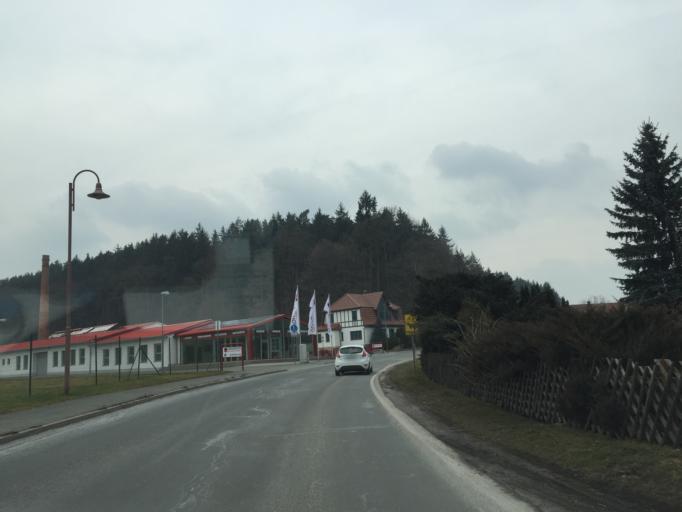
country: DE
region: Thuringia
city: Kranichfeld
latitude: 50.8640
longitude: 11.2058
